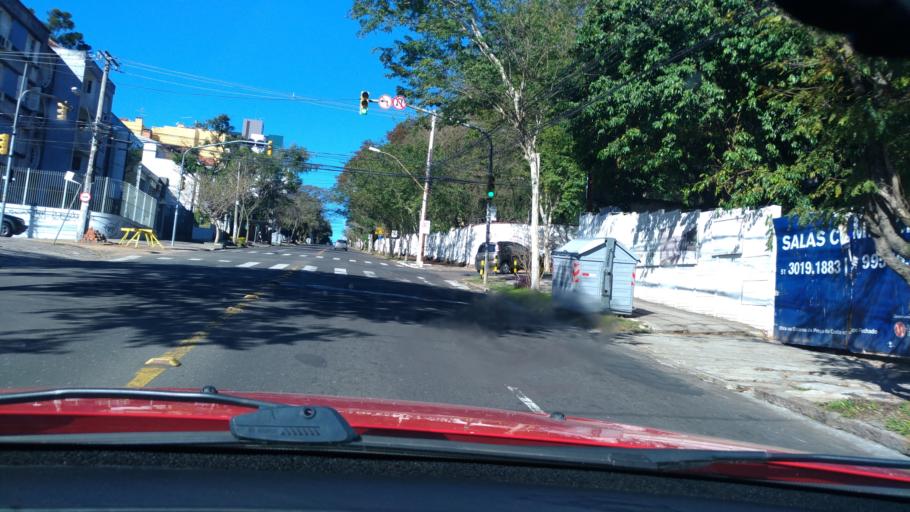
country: BR
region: Rio Grande do Sul
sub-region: Porto Alegre
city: Porto Alegre
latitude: -30.0178
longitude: -51.1947
